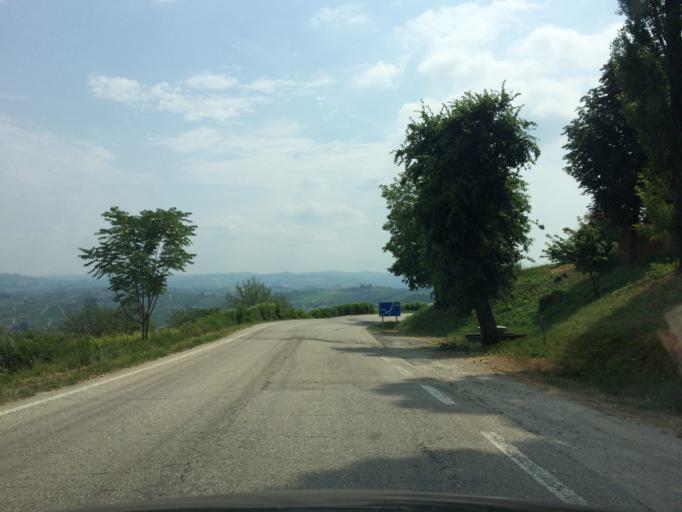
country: IT
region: Piedmont
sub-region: Provincia di Cuneo
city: Barolo
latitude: 44.6144
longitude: 7.9350
